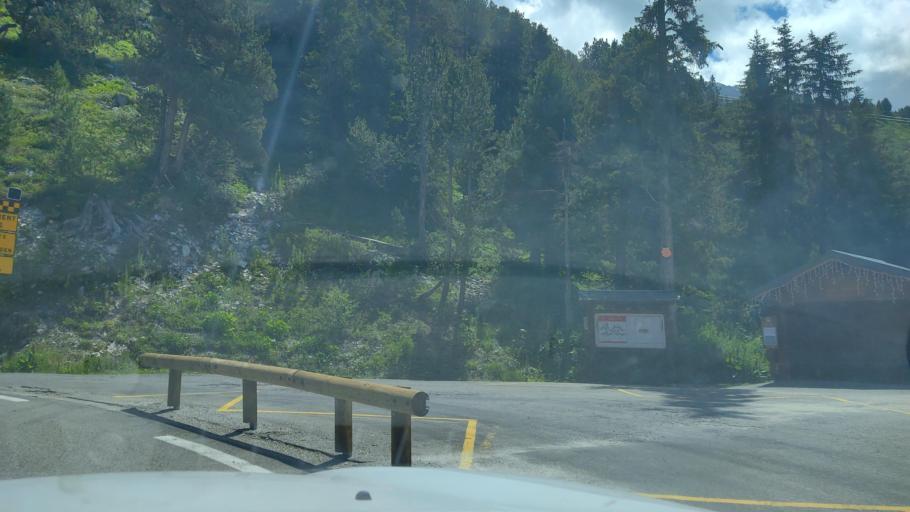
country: FR
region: Rhone-Alpes
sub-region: Departement de la Savoie
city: Seez
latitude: 45.5724
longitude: 6.8287
